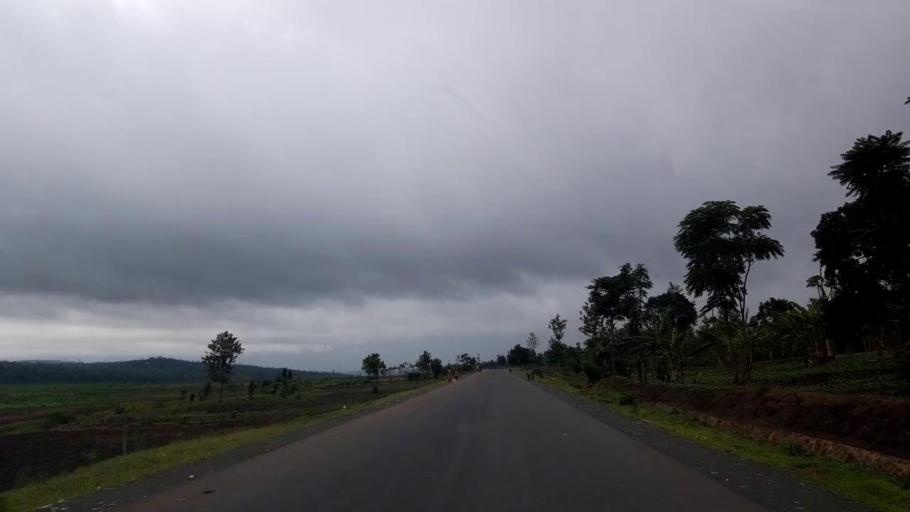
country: RW
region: Northern Province
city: Byumba
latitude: -1.4409
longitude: 30.2542
